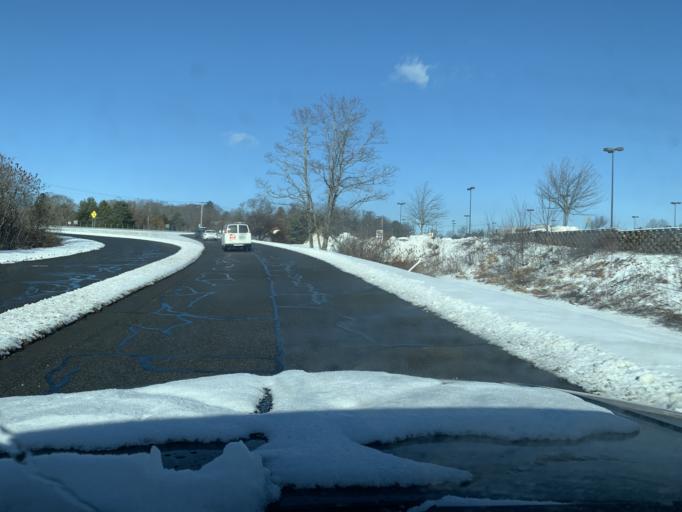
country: US
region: Massachusetts
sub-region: Essex County
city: Danvers
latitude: 42.5839
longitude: -70.9656
